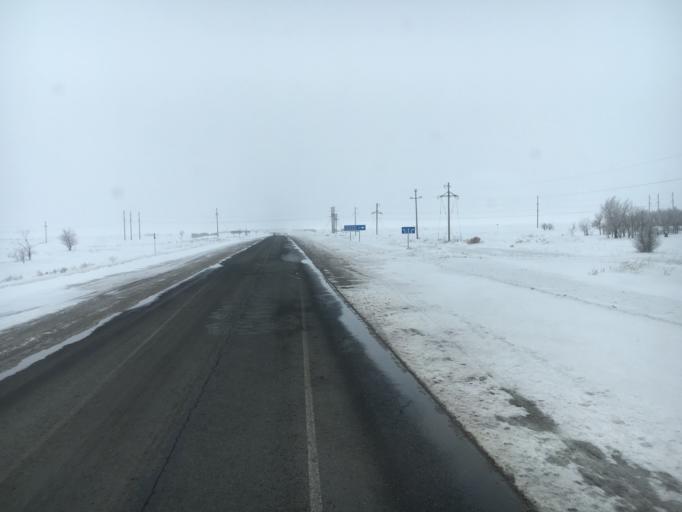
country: KZ
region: Batys Qazaqstan
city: Fedorovka
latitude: 50.7613
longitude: 51.9136
